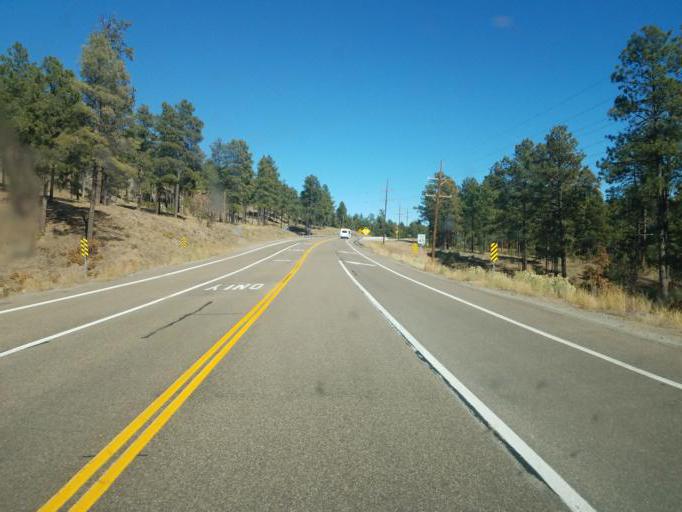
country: US
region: New Mexico
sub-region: Los Alamos County
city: Los Alamos
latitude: 35.8705
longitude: -106.3496
